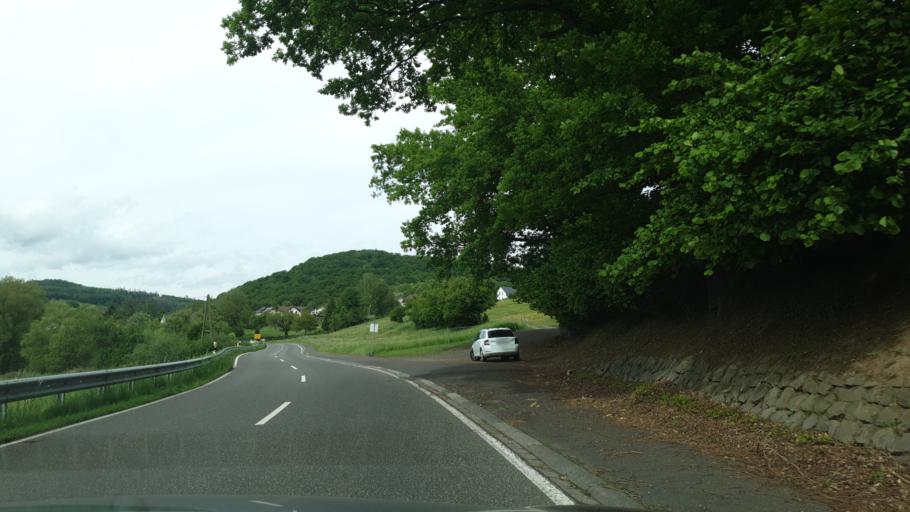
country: DE
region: Rheinland-Pfalz
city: Isselbach
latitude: 50.3840
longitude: 7.8882
